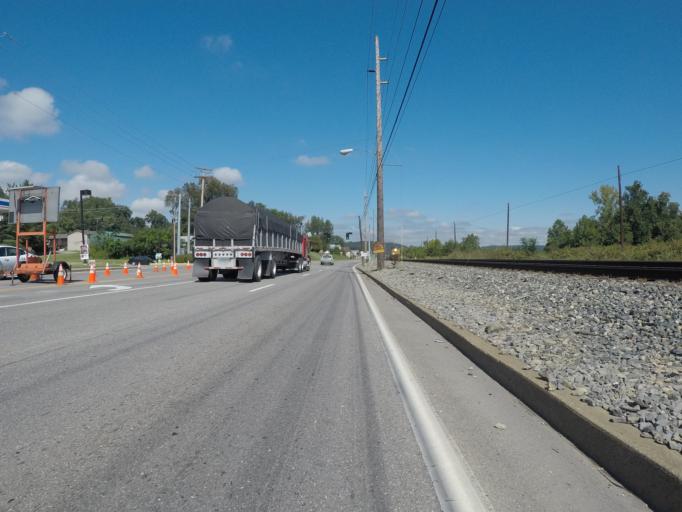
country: US
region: Ohio
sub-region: Lawrence County
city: South Point
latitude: 38.4388
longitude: -82.6086
